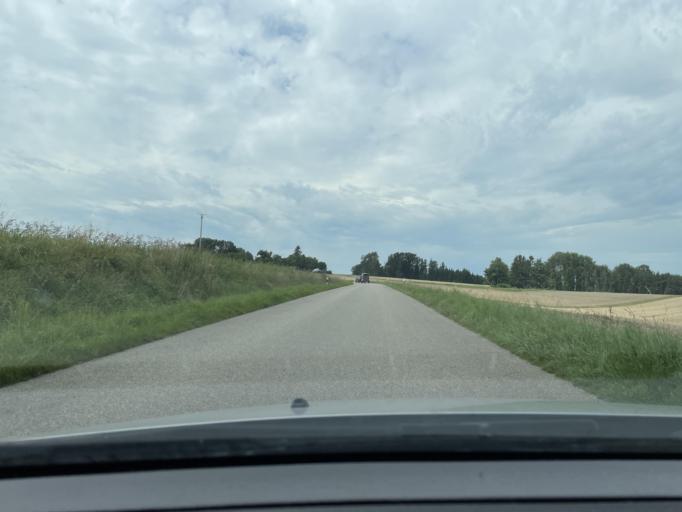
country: DE
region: Bavaria
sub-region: Lower Bavaria
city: Eging
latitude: 48.4495
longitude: 12.2108
